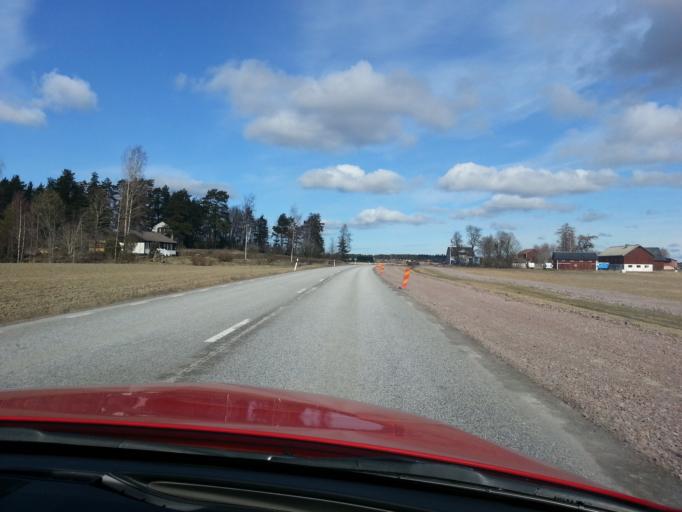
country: SE
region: Uppsala
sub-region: Osthammars Kommun
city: Gimo
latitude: 60.0447
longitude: 18.0450
